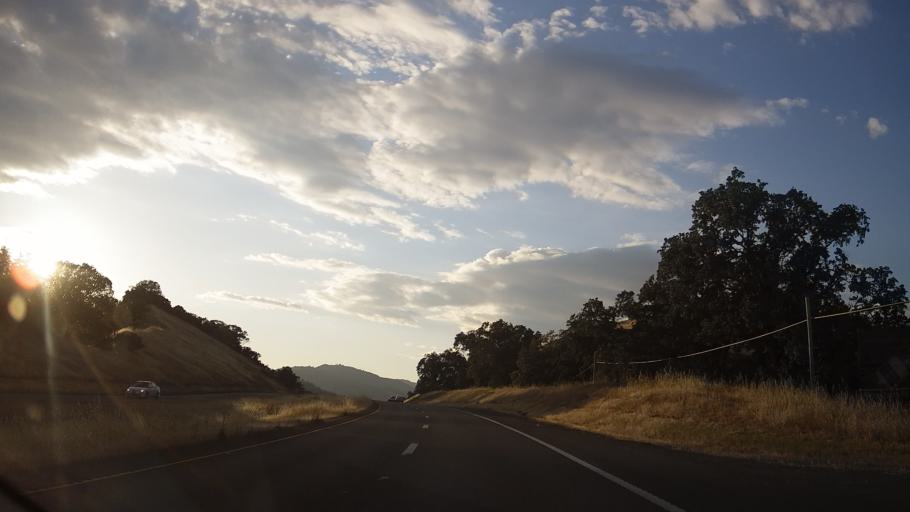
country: US
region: California
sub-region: Mendocino County
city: Talmage
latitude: 39.0708
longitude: -123.1700
